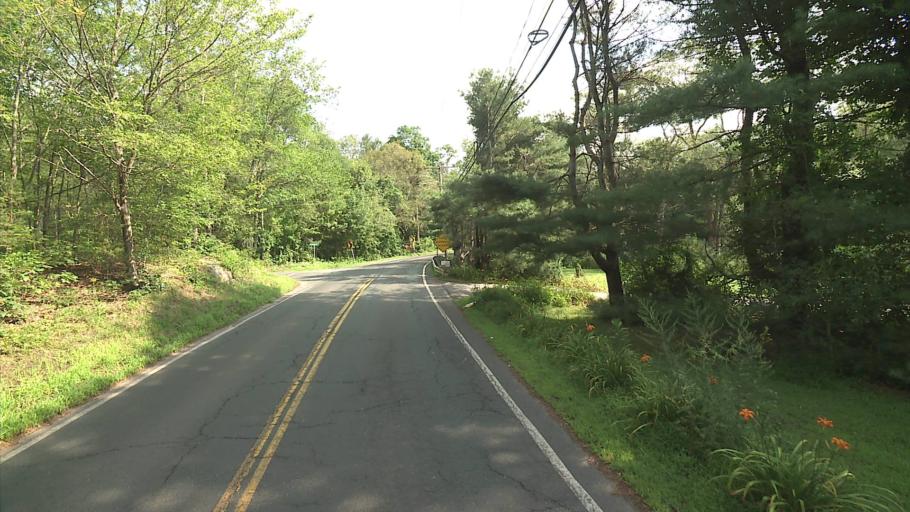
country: US
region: Connecticut
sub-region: Middlesex County
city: Moodus
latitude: 41.5148
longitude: -72.4273
